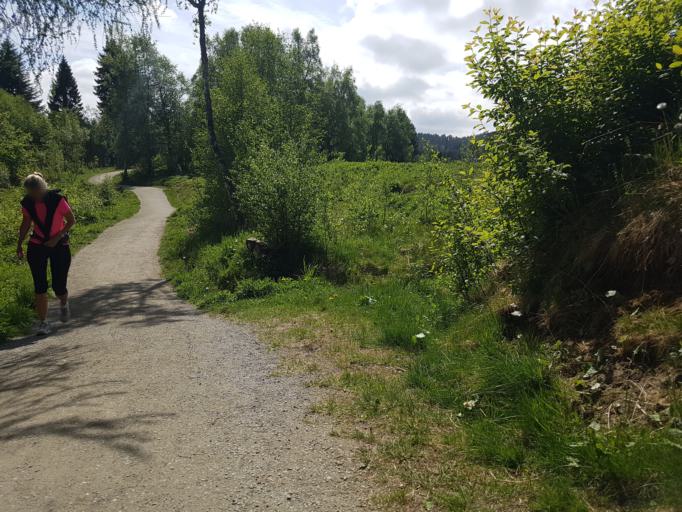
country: NO
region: Sor-Trondelag
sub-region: Trondheim
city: Trondheim
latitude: 63.4215
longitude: 10.3419
